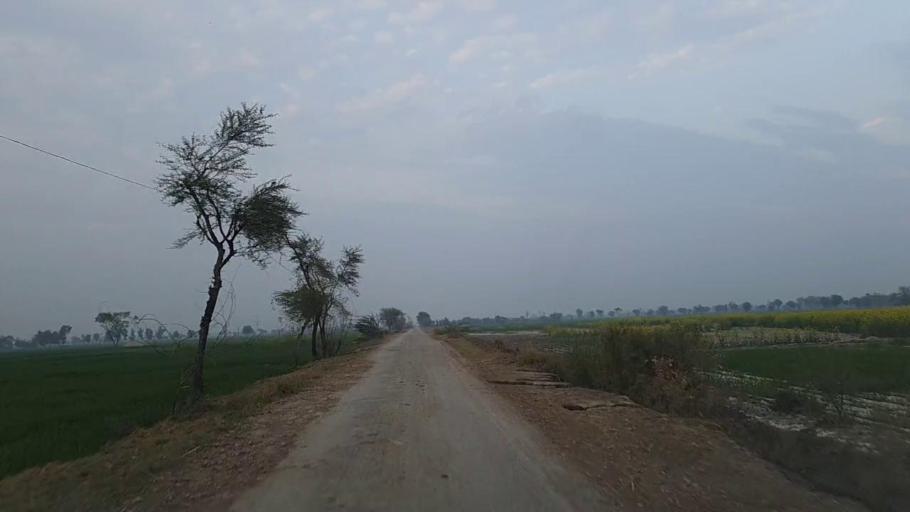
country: PK
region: Sindh
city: Jam Sahib
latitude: 26.3012
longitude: 68.5936
